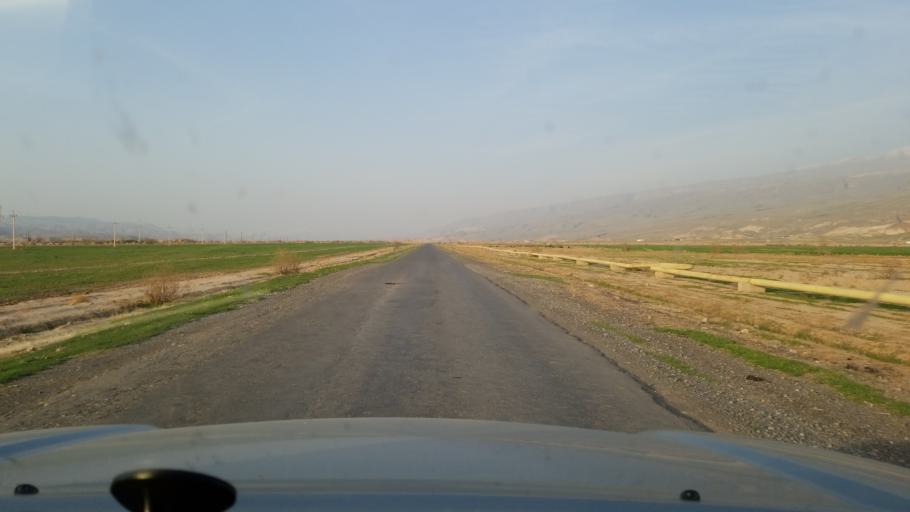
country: TM
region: Lebap
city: Gowurdak
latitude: 37.7638
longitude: 66.3614
